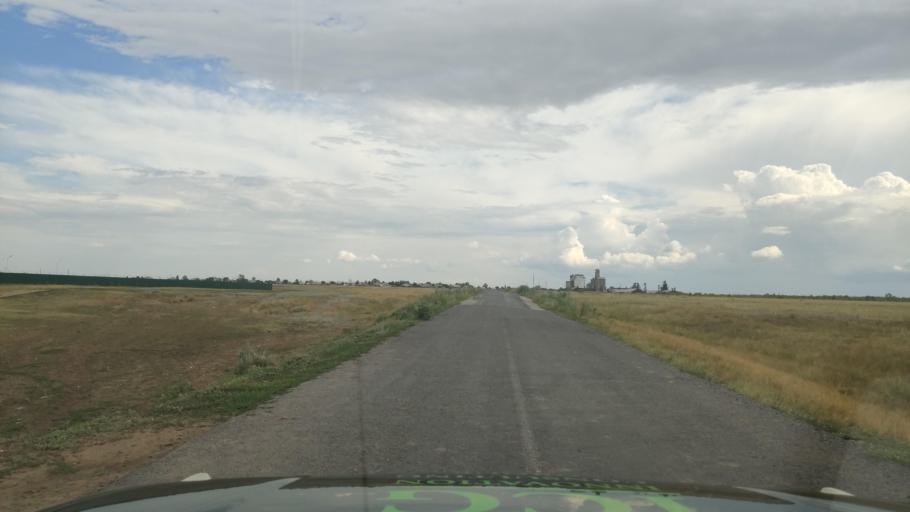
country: KZ
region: Pavlodar
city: Pavlodar
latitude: 52.6611
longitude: 77.4965
